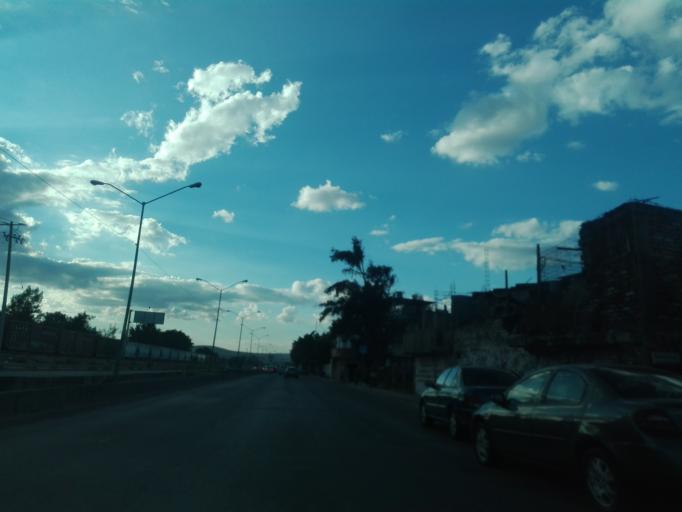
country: MX
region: Guanajuato
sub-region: Leon
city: San Jose de Duran (Los Troncoso)
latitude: 21.0850
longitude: -101.6670
